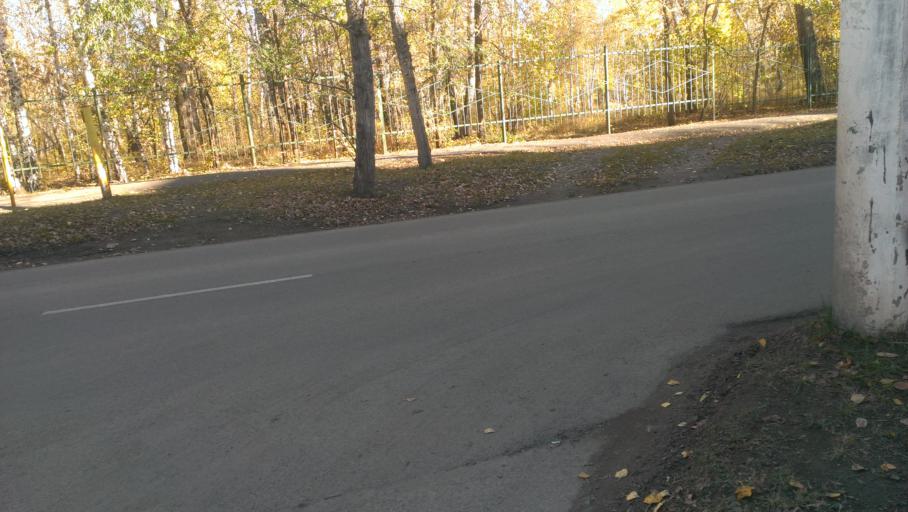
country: RU
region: Altai Krai
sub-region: Gorod Barnaulskiy
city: Barnaul
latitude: 53.3640
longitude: 83.6878
